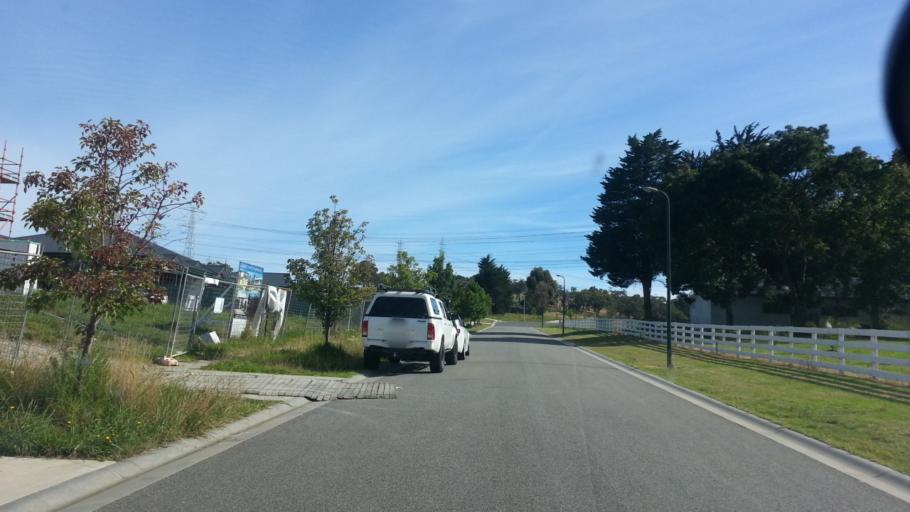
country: AU
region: Victoria
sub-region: Casey
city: Narre Warren North
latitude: -37.9780
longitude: 145.2898
